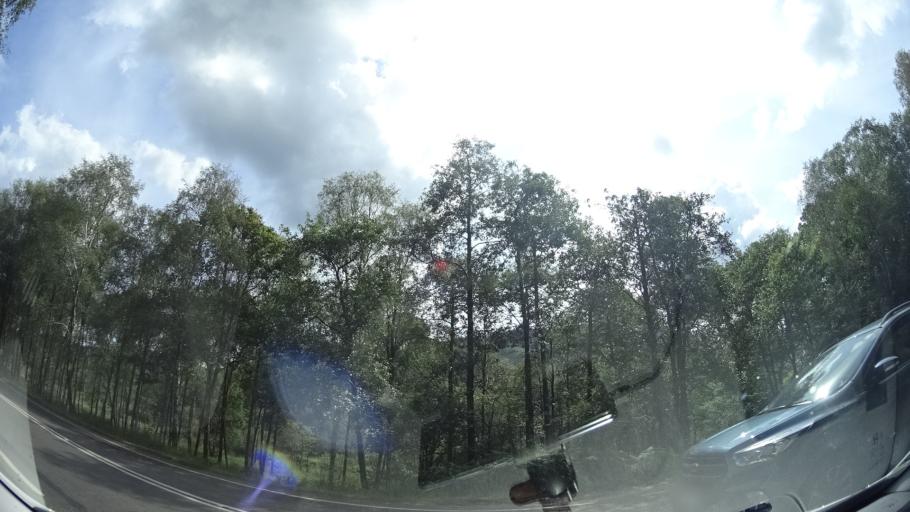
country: GB
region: Scotland
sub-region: Highland
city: Fort William
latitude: 56.8683
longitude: -5.4319
